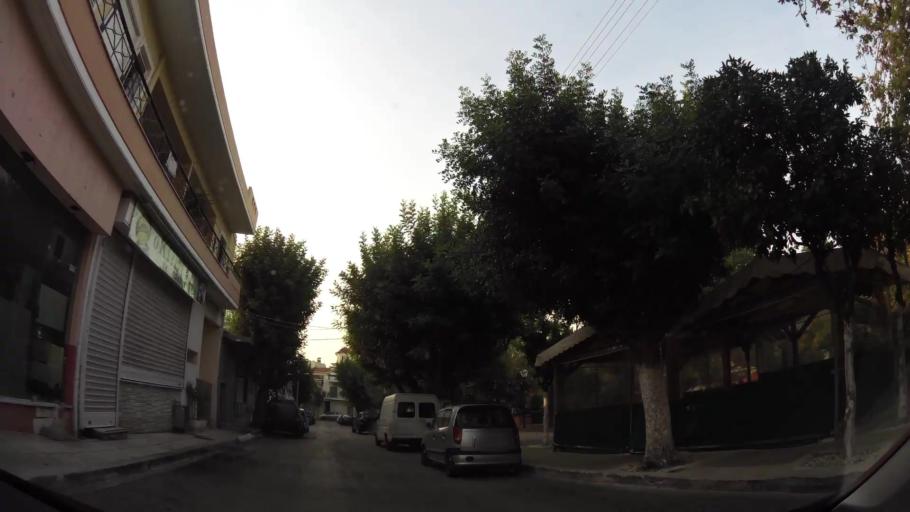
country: GR
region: Attica
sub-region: Nomarchia Athinas
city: Peristeri
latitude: 38.0223
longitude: 23.6898
